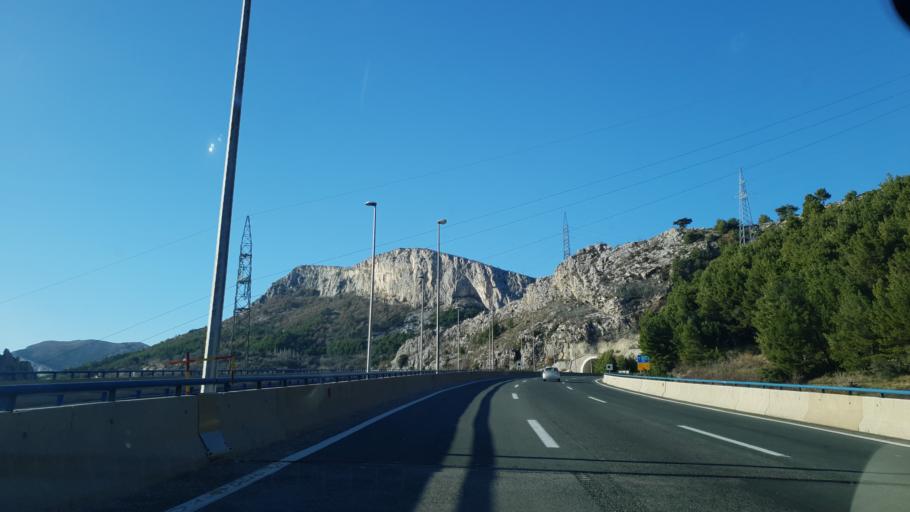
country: HR
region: Splitsko-Dalmatinska
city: Klis
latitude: 43.5608
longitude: 16.5345
